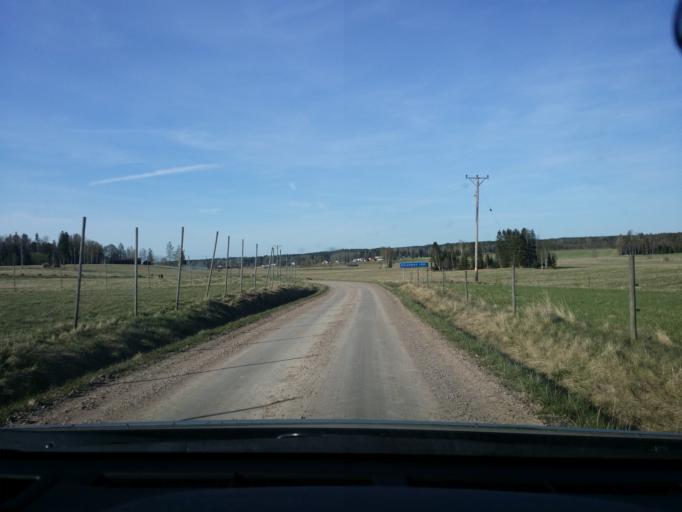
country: SE
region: Dalarna
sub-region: Avesta Kommun
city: Avesta
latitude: 60.0793
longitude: 16.3697
